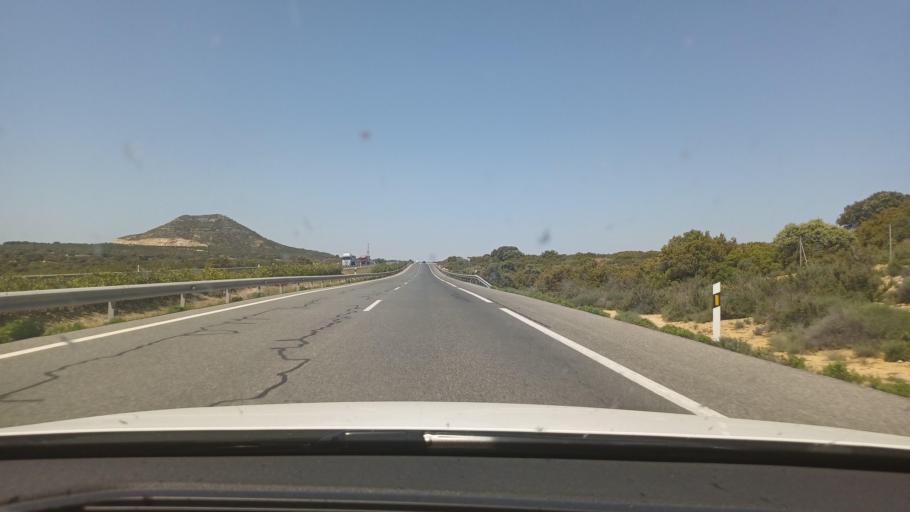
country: ES
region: Castille-La Mancha
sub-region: Provincia de Albacete
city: Corral-Rubio
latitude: 38.8981
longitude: -1.4464
